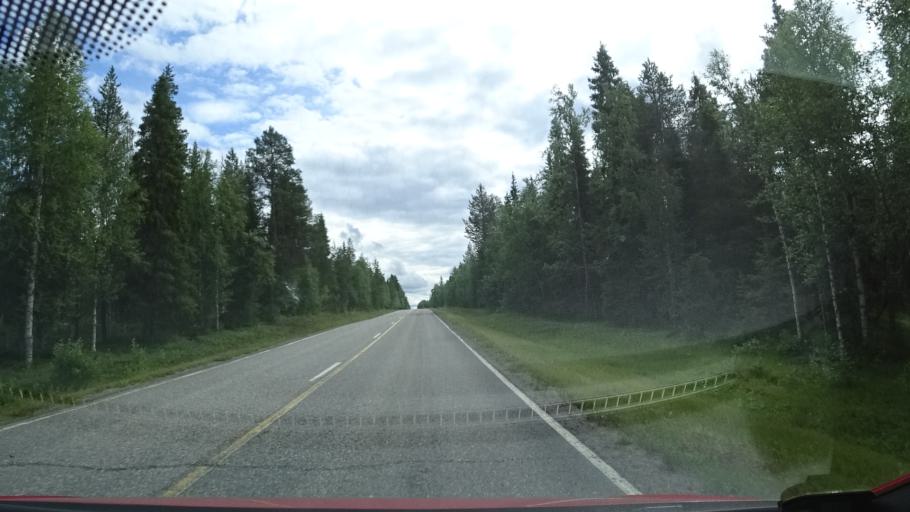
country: FI
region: Lapland
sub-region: Tunturi-Lappi
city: Kittilae
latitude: 67.4747
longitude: 24.9371
